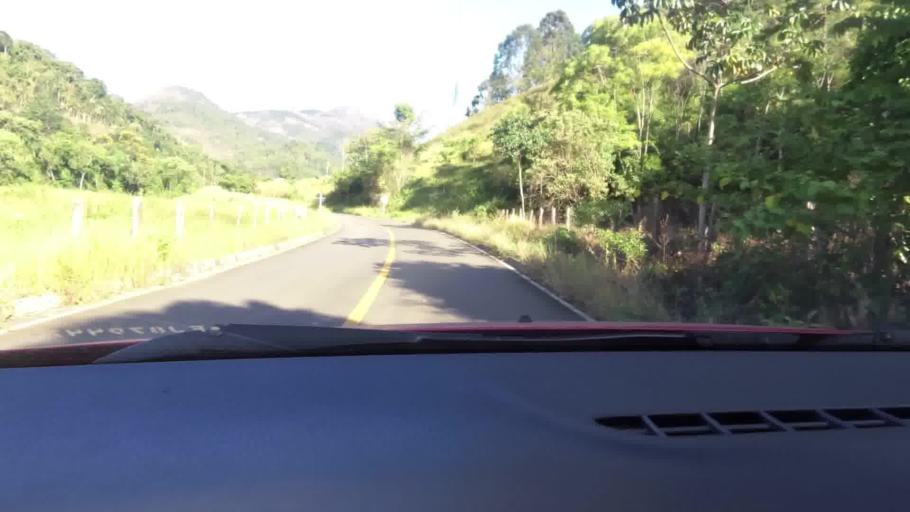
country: BR
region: Espirito Santo
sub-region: Guarapari
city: Guarapari
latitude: -20.5729
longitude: -40.5441
